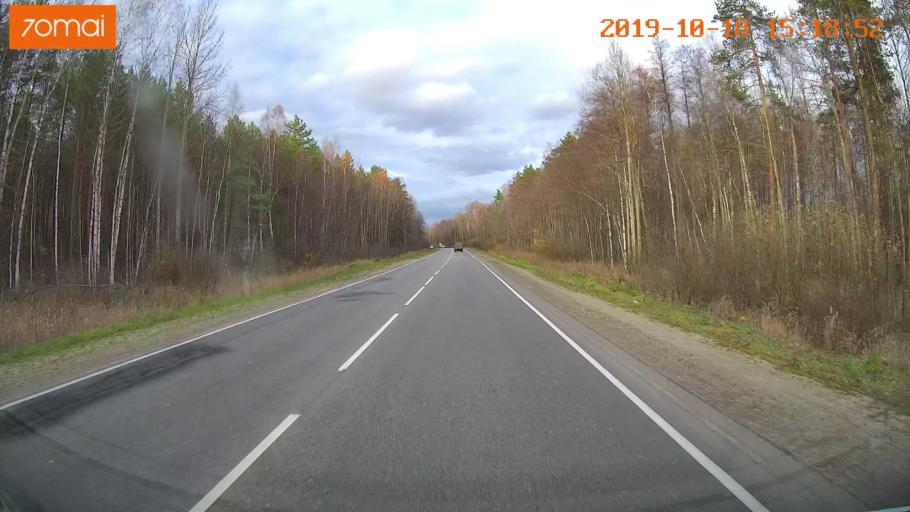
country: RU
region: Vladimir
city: Anopino
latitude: 55.6649
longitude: 40.7330
